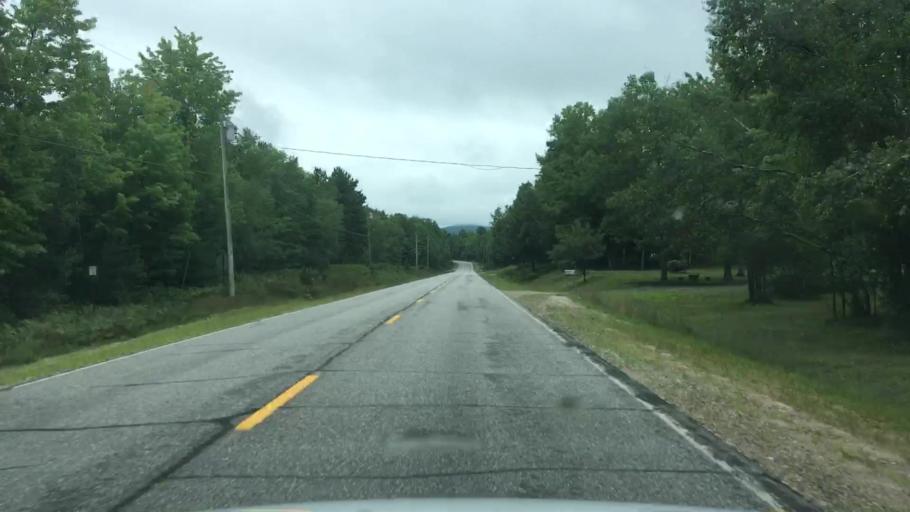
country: US
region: Maine
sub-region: Oxford County
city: Brownfield
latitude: 43.9365
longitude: -70.8852
